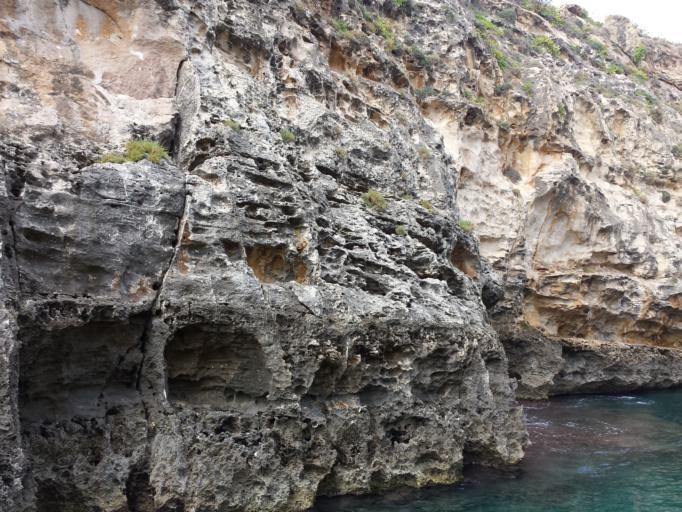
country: MT
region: Iz-Zebbug
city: Zebbug
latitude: 36.0797
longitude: 14.2288
